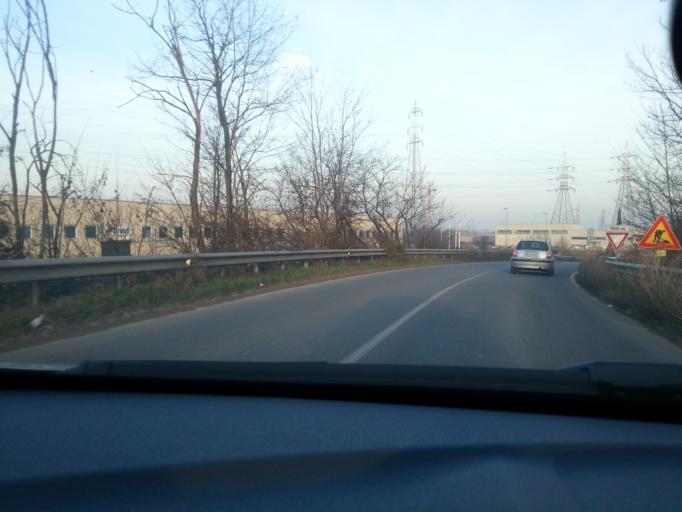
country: IT
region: Lombardy
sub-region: Citta metropolitana di Milano
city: Arese
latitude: 45.5372
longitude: 9.0812
